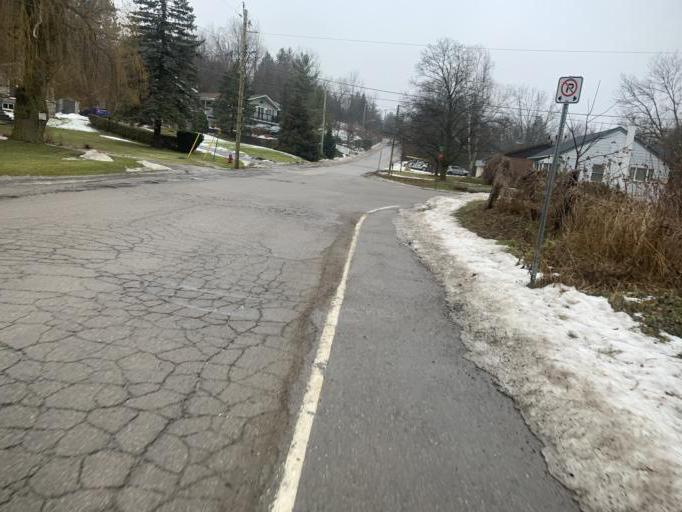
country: CA
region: Ontario
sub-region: Halton
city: Milton
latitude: 43.6579
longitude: -79.9336
